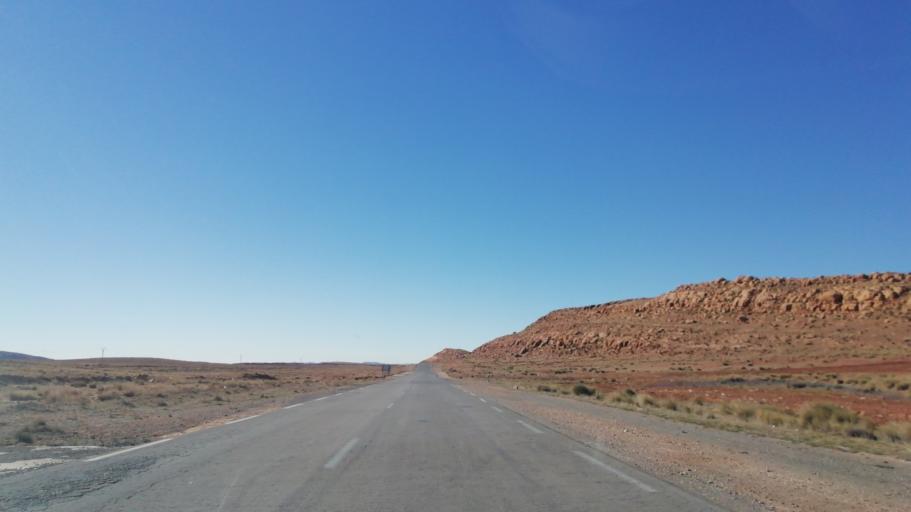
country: DZ
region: El Bayadh
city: El Bayadh
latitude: 33.6580
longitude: 1.4184
